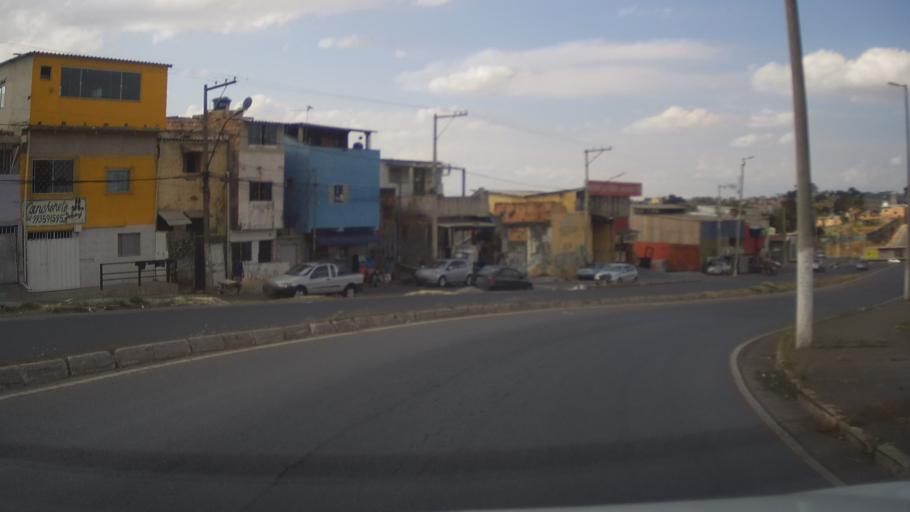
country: BR
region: Minas Gerais
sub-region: Belo Horizonte
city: Belo Horizonte
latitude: -19.8790
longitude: -43.9538
